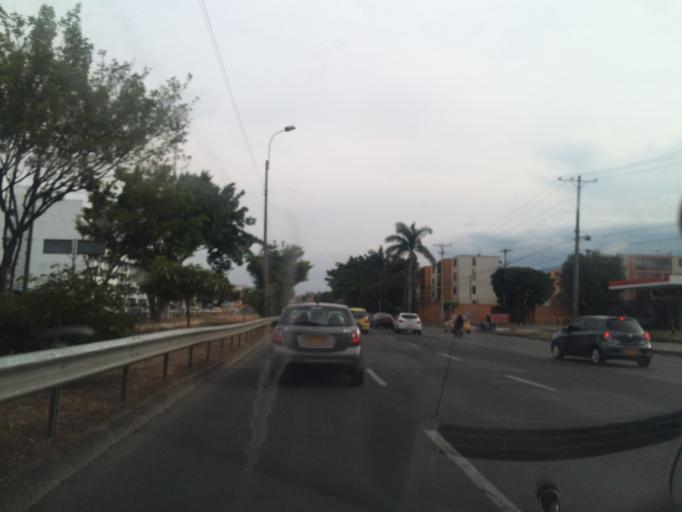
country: CO
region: Valle del Cauca
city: Cali
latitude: 3.4092
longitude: -76.5392
